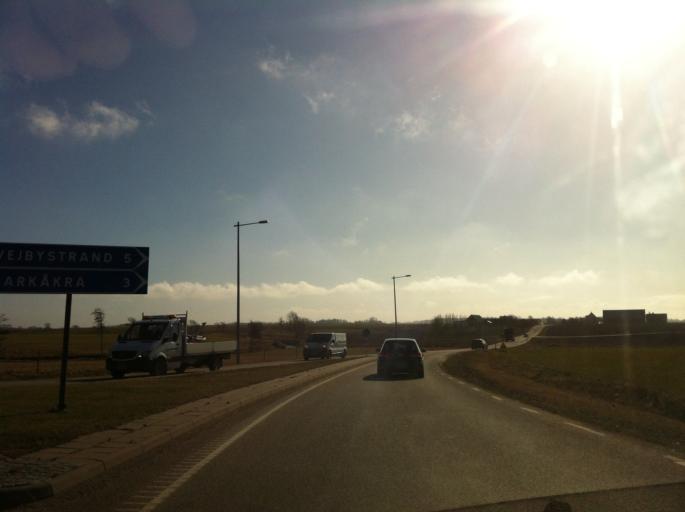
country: SE
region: Skane
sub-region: Bastads Kommun
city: Forslov
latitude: 56.3245
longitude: 12.8395
